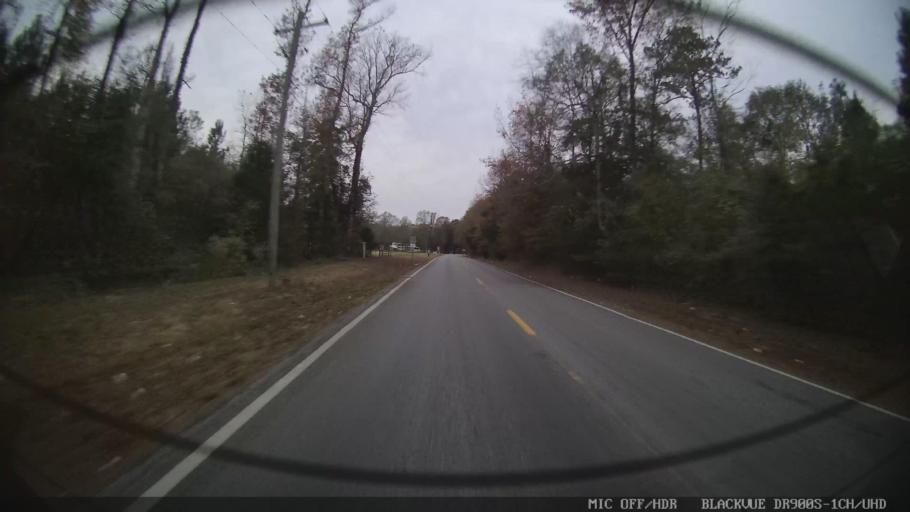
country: US
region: Mississippi
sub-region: Clarke County
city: Quitman
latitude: 32.0234
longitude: -88.8483
